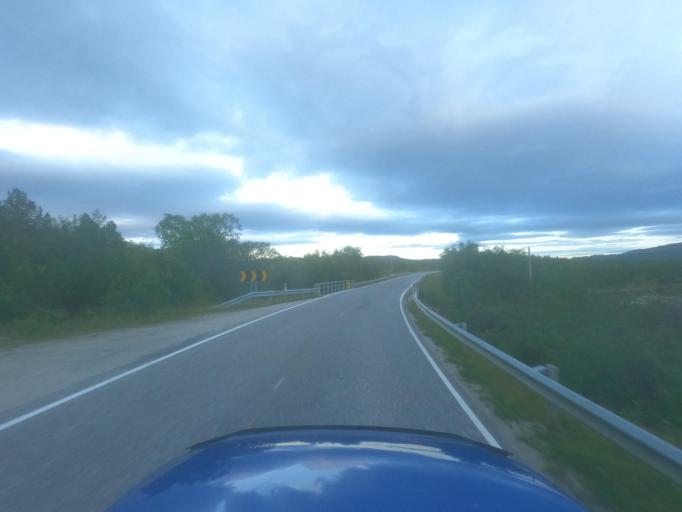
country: NO
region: Finnmark Fylke
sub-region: Porsanger
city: Lakselv
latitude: 69.9105
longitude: 24.9930
